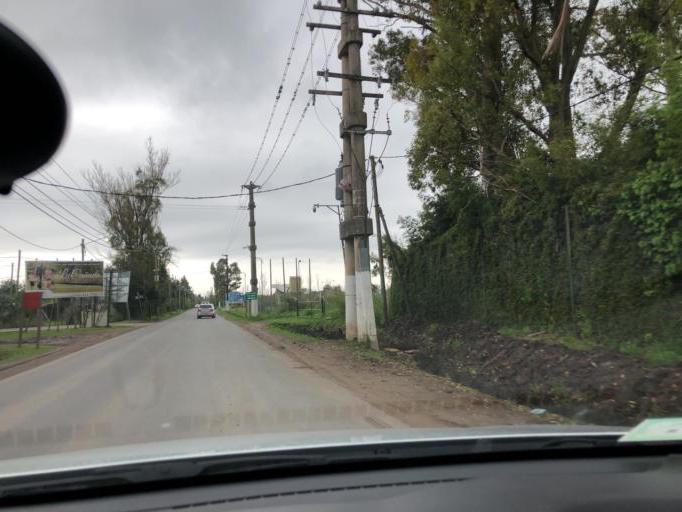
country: AR
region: Buenos Aires
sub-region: Partido de La Plata
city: La Plata
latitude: -34.9025
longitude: -58.0698
